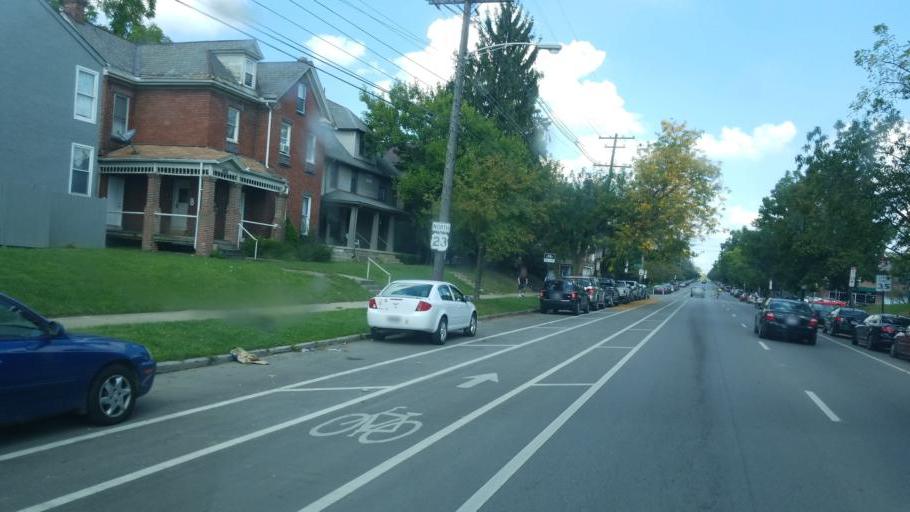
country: US
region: Ohio
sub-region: Franklin County
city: Columbus
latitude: 40.0014
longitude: -82.9986
